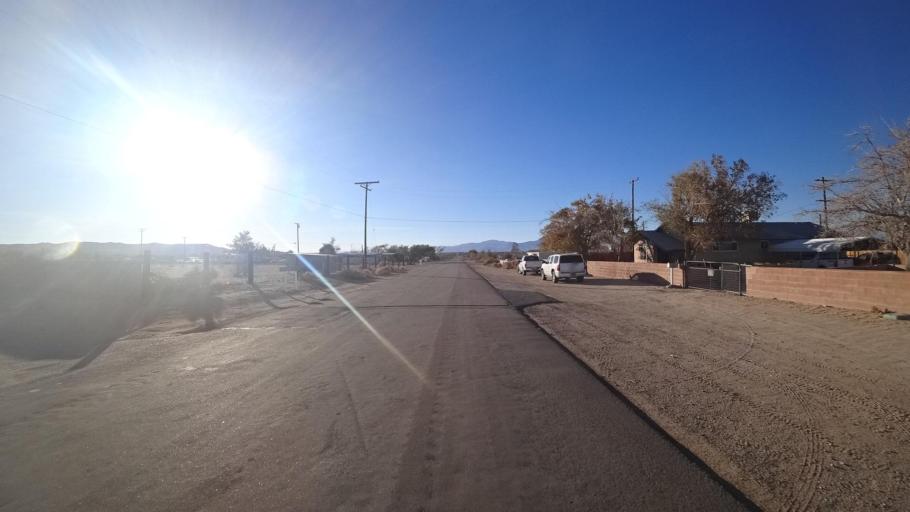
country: US
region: California
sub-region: Kern County
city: Ridgecrest
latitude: 35.6007
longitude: -117.6562
